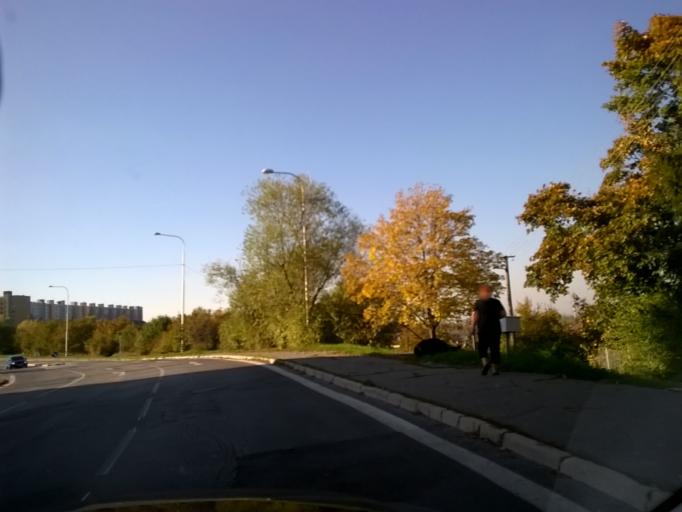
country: SK
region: Nitriansky
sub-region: Okres Nitra
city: Nitra
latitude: 48.3064
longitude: 18.0554
